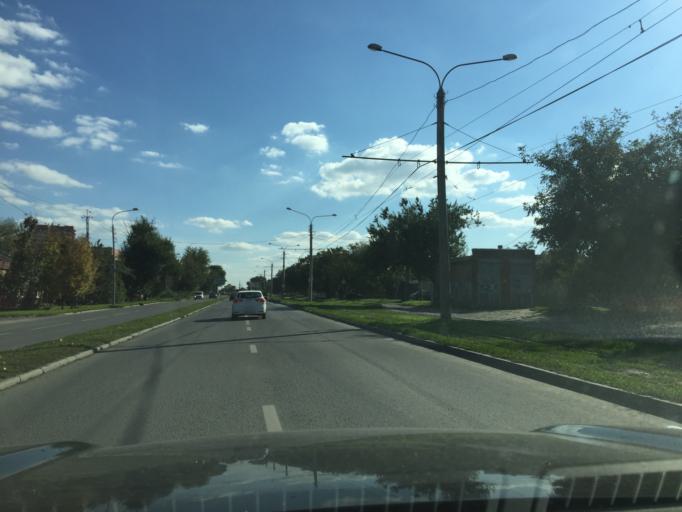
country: RU
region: Rostov
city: Rostov-na-Donu
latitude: 47.2188
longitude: 39.6456
